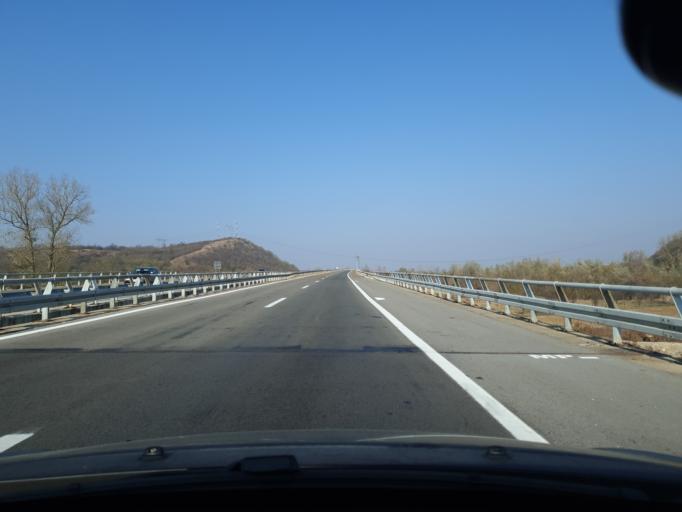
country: RS
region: Central Serbia
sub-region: Nisavski Okrug
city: Doljevac
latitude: 43.2132
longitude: 21.8364
